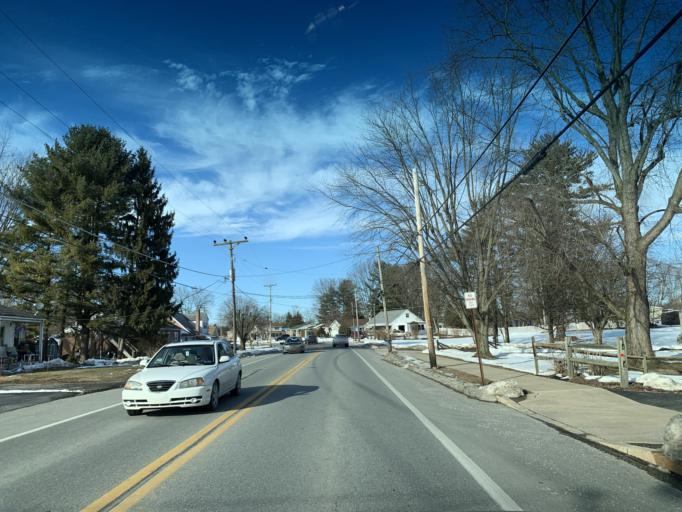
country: US
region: Pennsylvania
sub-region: York County
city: Dillsburg
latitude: 40.0999
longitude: -77.0309
